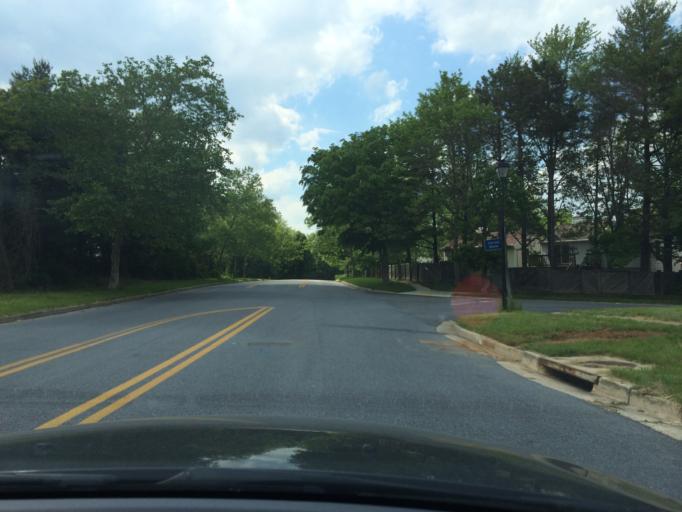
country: US
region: Maryland
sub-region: Howard County
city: Savage
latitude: 39.1776
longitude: -76.8413
